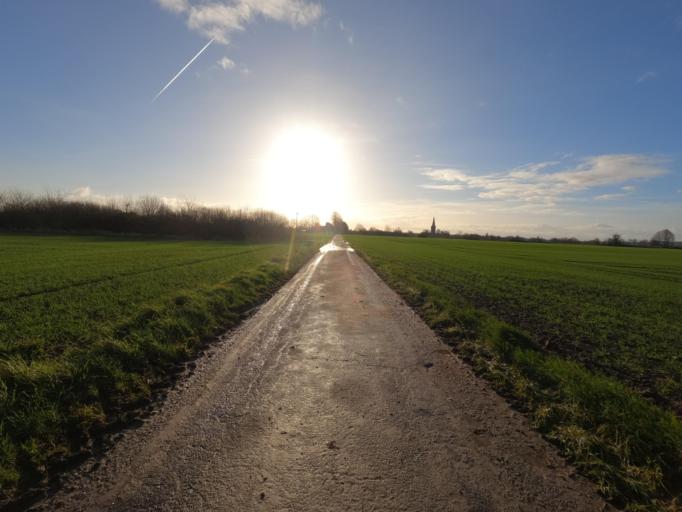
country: DE
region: North Rhine-Westphalia
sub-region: Regierungsbezirk Koln
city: Bedburg
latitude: 50.9723
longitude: 6.5398
